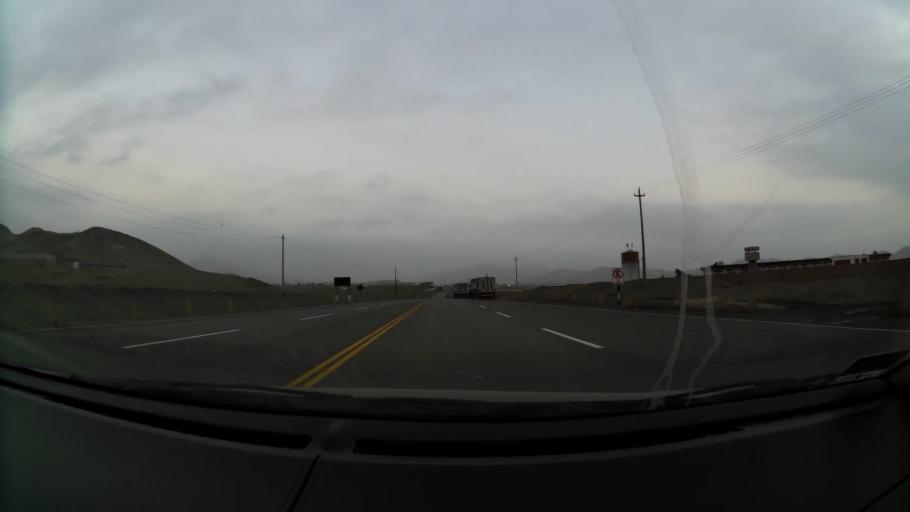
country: PE
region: Lima
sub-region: Lima
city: Santa Rosa
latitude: -11.7450
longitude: -77.1646
